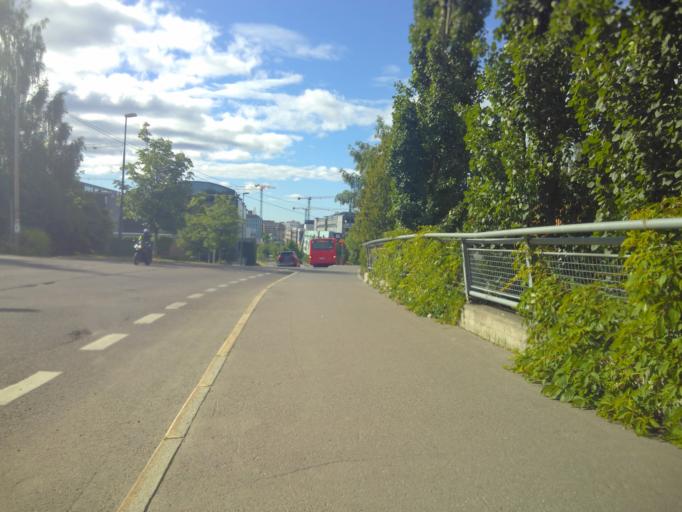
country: NO
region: Oslo
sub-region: Oslo
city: Oslo
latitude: 59.9512
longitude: 10.7680
